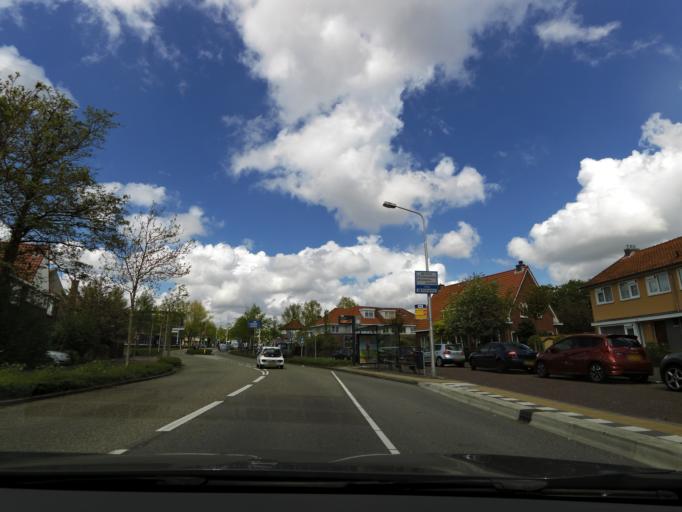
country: NL
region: North Holland
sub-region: Gemeente Amstelveen
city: Amstelveen
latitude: 52.2981
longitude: 4.8550
